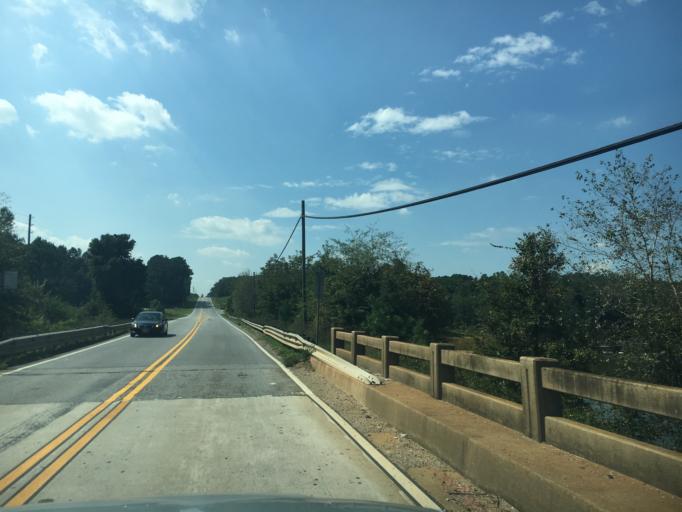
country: US
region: Georgia
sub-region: Hart County
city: Hartwell
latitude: 34.3613
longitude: -82.9542
